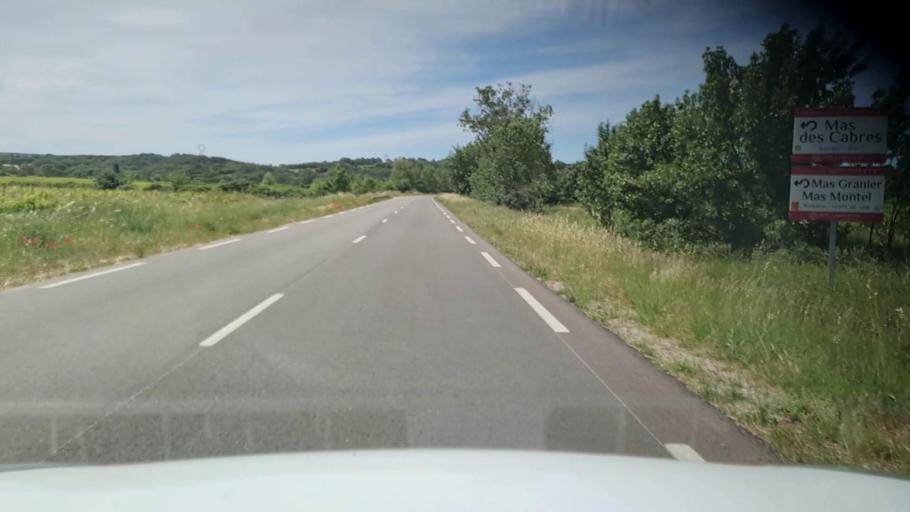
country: FR
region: Languedoc-Roussillon
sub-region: Departement du Gard
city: Sommieres
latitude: 43.8084
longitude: 4.0645
